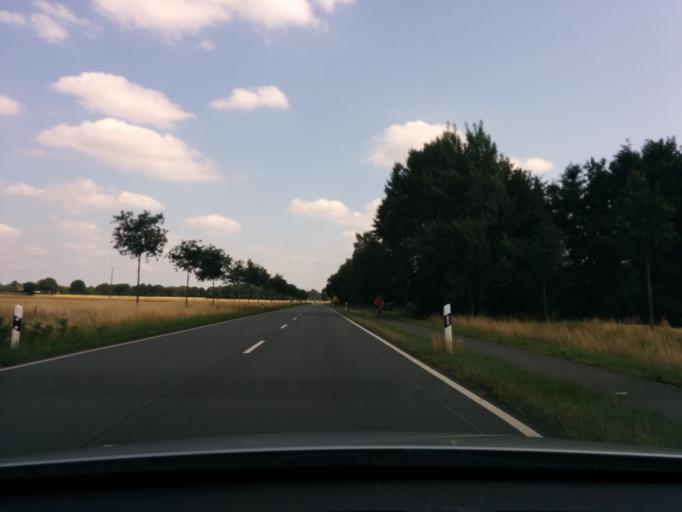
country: DE
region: North Rhine-Westphalia
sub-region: Regierungsbezirk Munster
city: Wettringen
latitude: 52.1840
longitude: 7.2671
